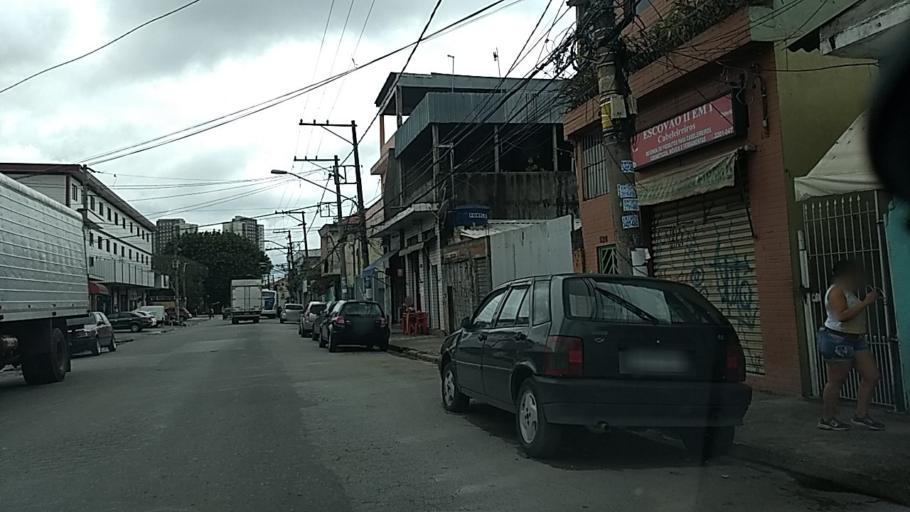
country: BR
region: Sao Paulo
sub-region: Guarulhos
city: Guarulhos
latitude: -23.4883
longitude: -46.5689
